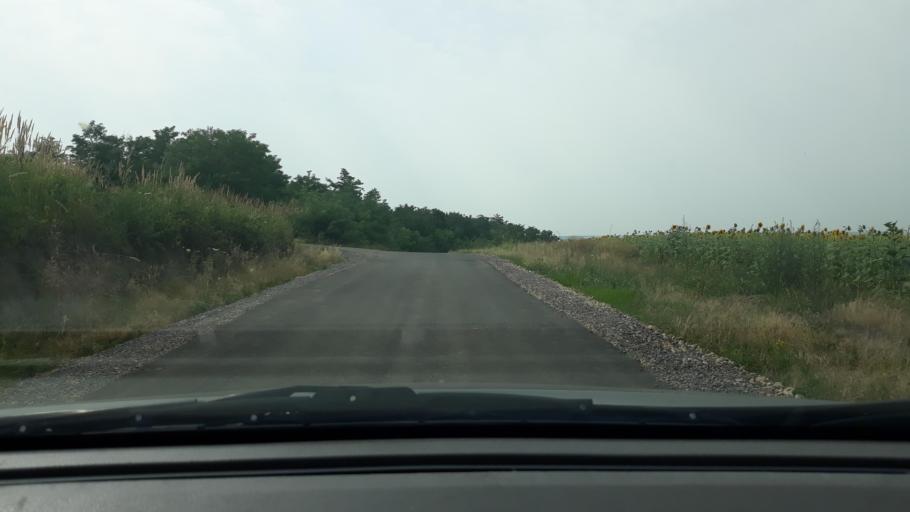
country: RO
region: Bihor
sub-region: Comuna Chislaz
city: Misca
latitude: 47.2613
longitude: 22.2935
